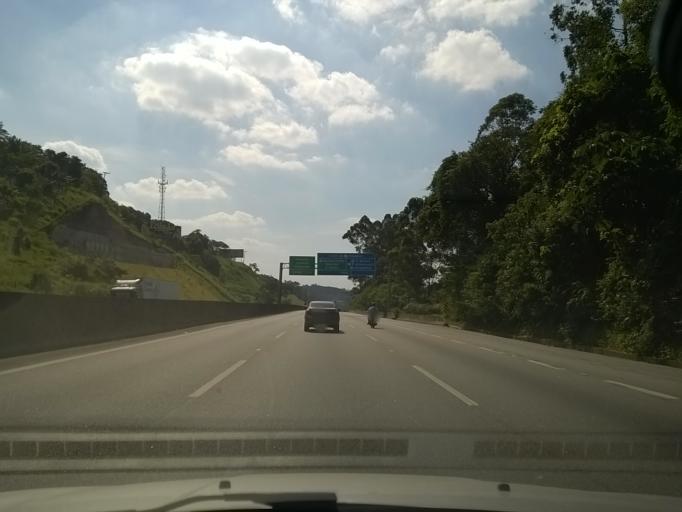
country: BR
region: Sao Paulo
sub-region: Osasco
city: Osasco
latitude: -23.4629
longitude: -46.7796
